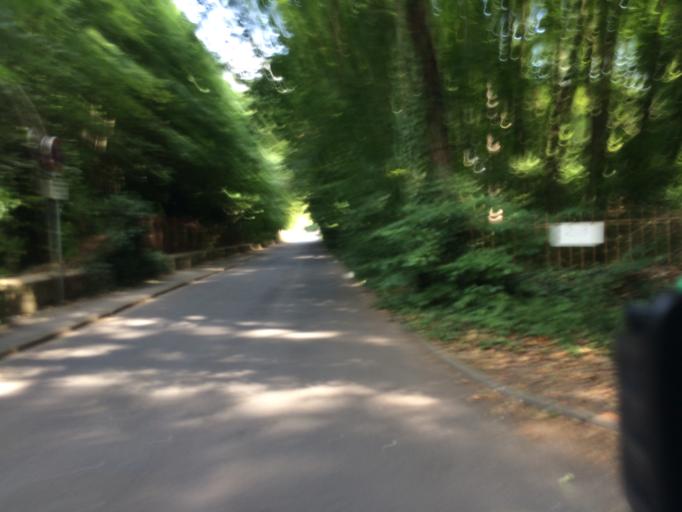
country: FR
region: Ile-de-France
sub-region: Departement de l'Essonne
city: Ris-Orangis
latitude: 48.6612
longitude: 2.4197
